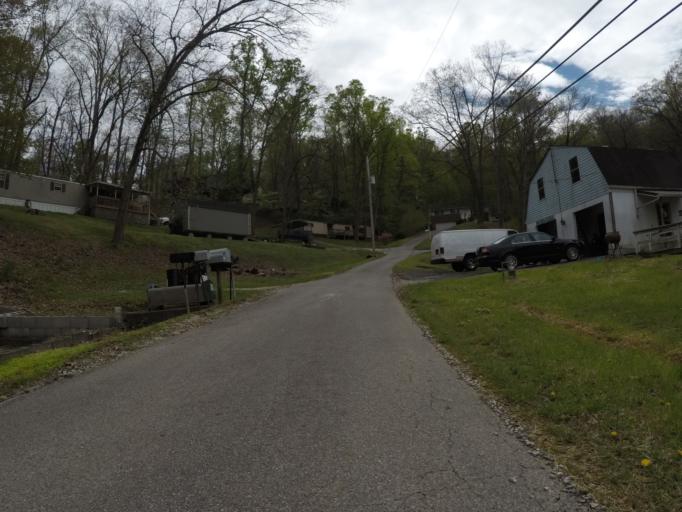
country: US
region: Ohio
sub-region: Lawrence County
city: Burlington
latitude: 38.3914
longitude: -82.5170
